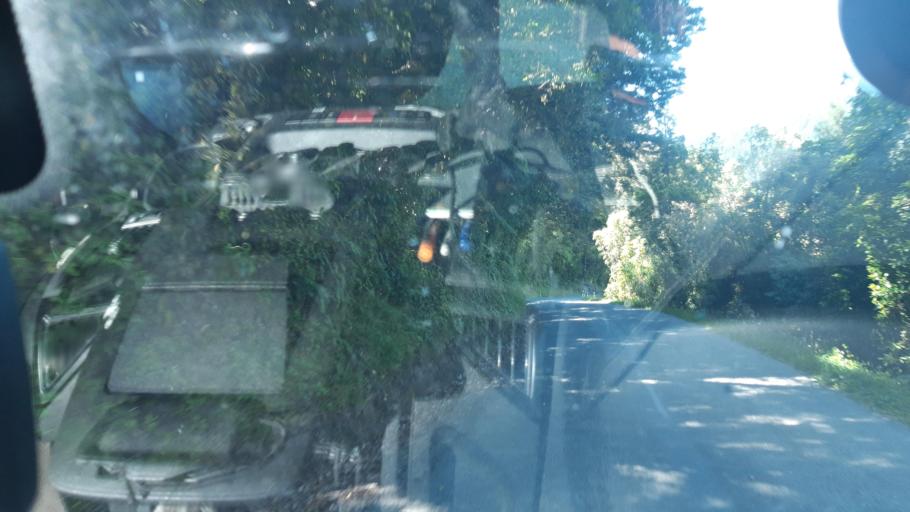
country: NZ
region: Tasman
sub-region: Tasman District
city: Motueka
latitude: -41.0477
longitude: 172.9268
